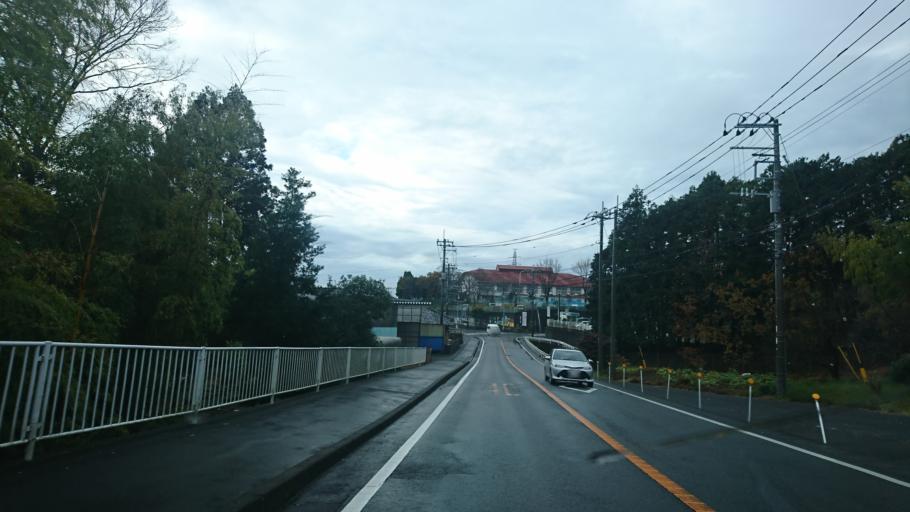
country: JP
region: Shizuoka
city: Fuji
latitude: 35.1941
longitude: 138.7246
